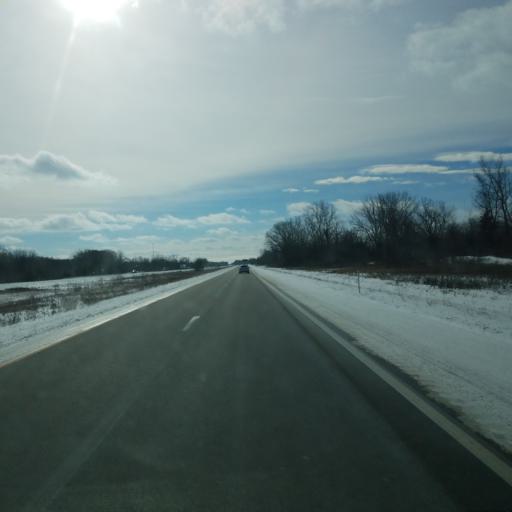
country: US
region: Michigan
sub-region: Gratiot County
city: Saint Louis
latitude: 43.3580
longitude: -84.6018
